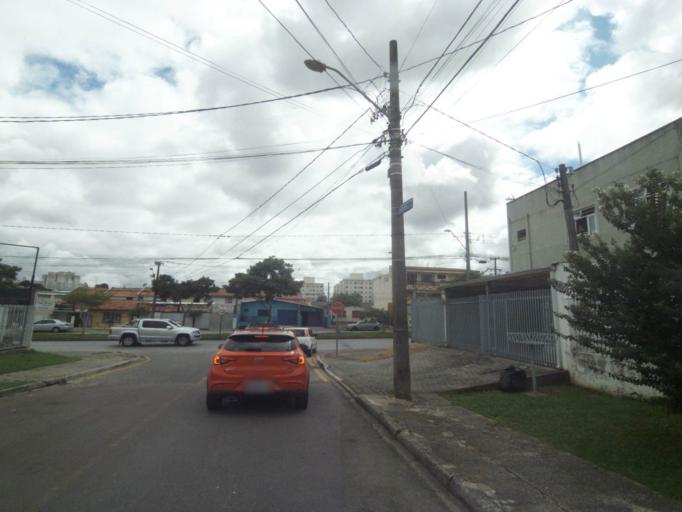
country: BR
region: Parana
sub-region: Curitiba
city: Curitiba
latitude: -25.4818
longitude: -49.2737
